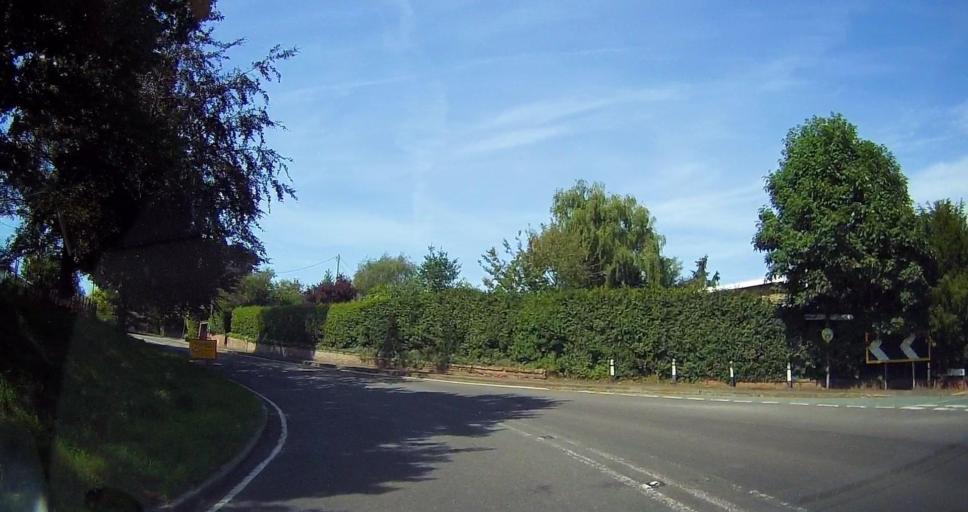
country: GB
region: England
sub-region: Shropshire
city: Market Drayton
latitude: 52.9569
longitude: -2.5051
